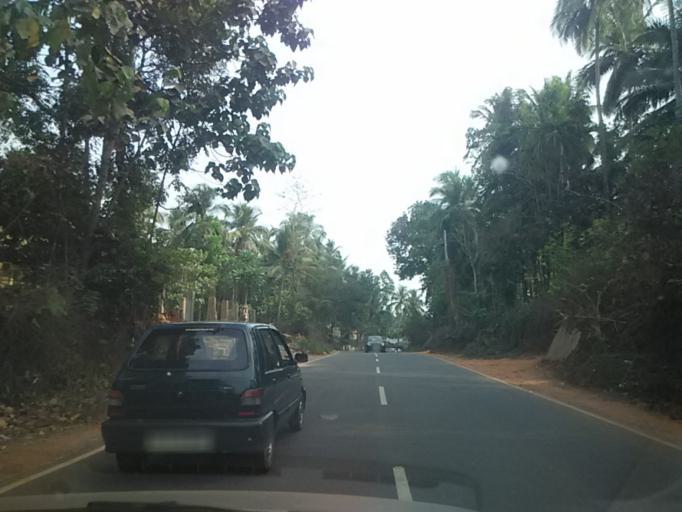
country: IN
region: Kerala
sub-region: Kozhikode
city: Naduvannur
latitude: 11.4927
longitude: 75.7748
